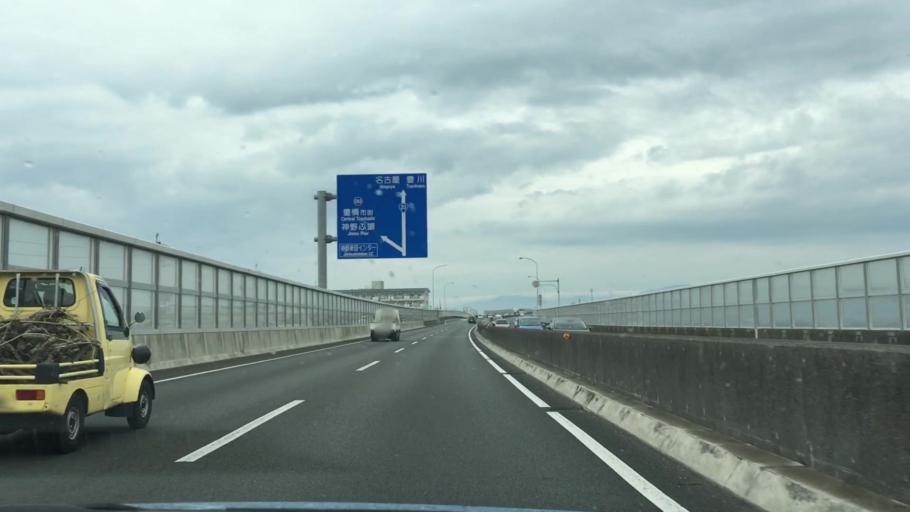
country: JP
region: Aichi
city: Toyohashi
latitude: 34.7355
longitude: 137.3473
